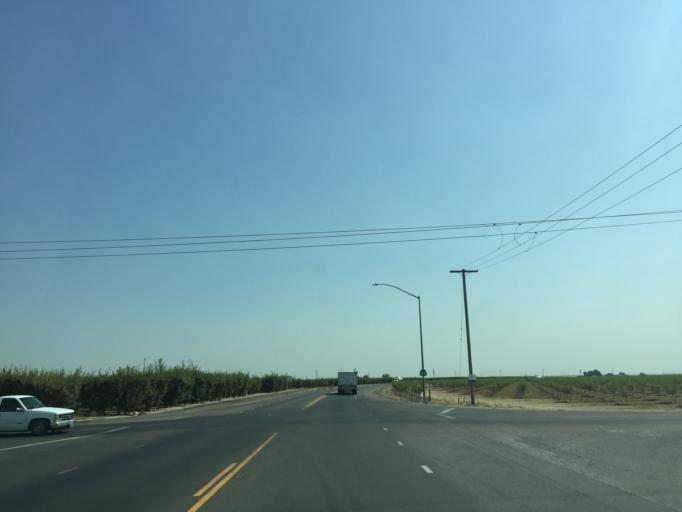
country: US
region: California
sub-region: Fresno County
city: Kingsburg
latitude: 36.4896
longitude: -119.6292
